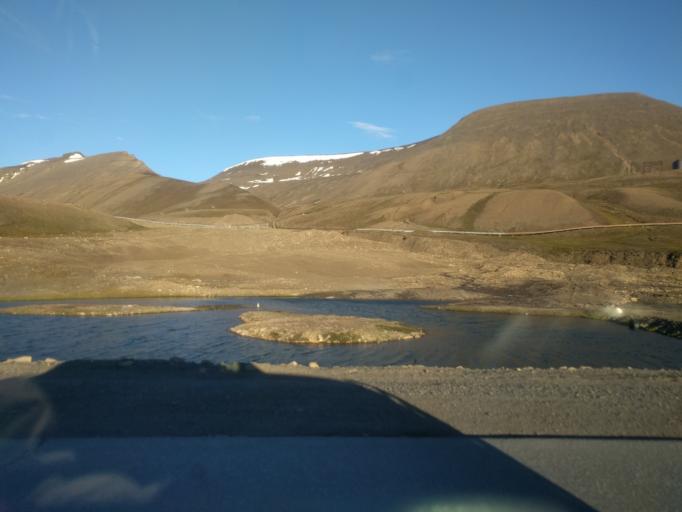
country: SJ
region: Svalbard
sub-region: Spitsbergen
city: Longyearbyen
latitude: 78.2190
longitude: 15.6922
